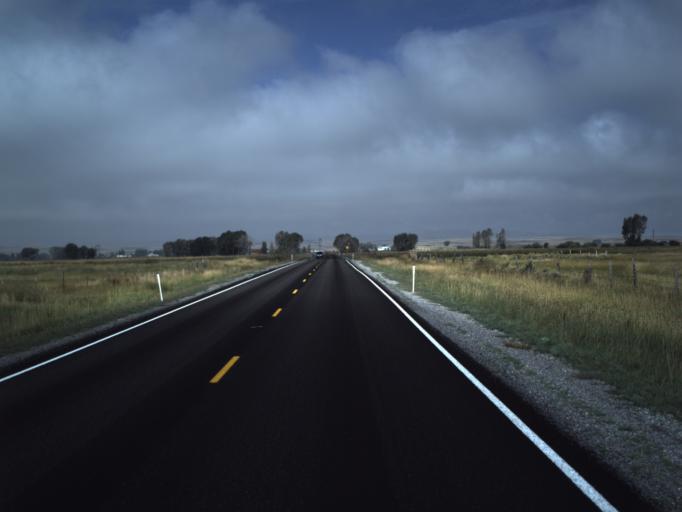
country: US
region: Utah
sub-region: Rich County
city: Randolph
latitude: 41.5135
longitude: -111.1342
